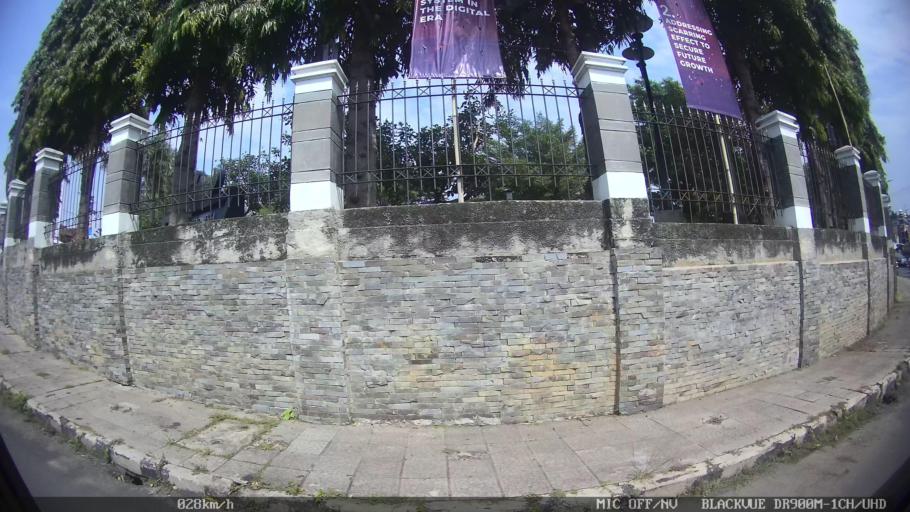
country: ID
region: Lampung
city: Bandarlampung
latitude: -5.4440
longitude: 105.2685
